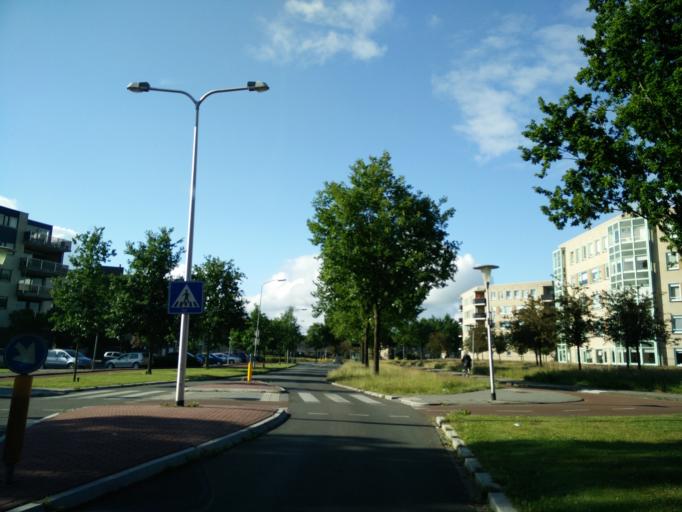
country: NL
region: Drenthe
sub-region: Gemeente Assen
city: Assen
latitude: 53.0182
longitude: 6.5840
